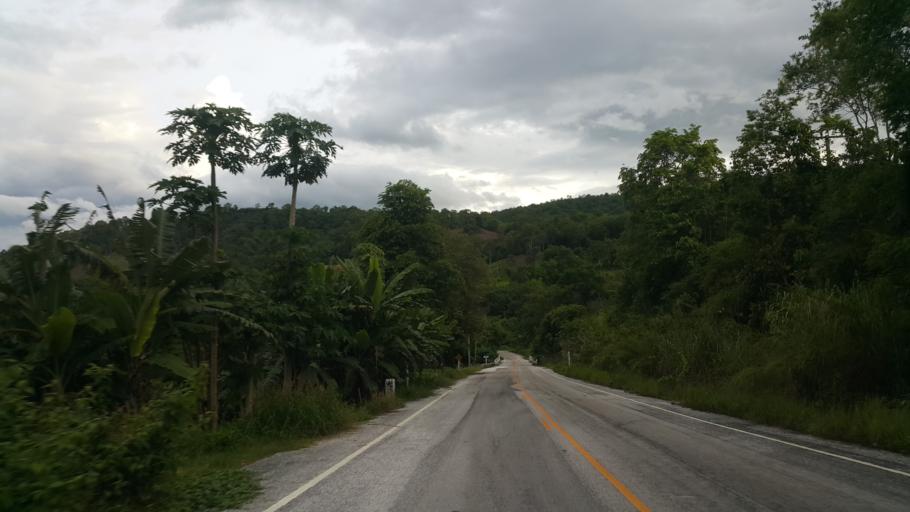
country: TH
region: Loei
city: Na Haeo
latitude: 17.4839
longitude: 101.1091
